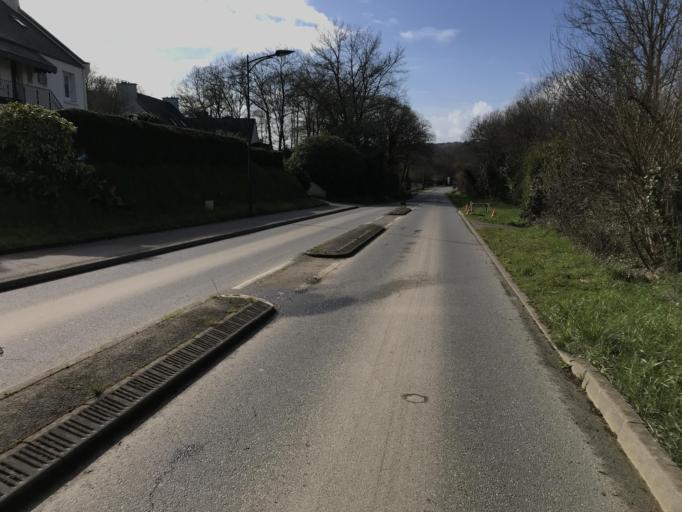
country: FR
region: Brittany
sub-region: Departement du Finistere
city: Loperhet
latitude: 48.3780
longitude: -4.3166
